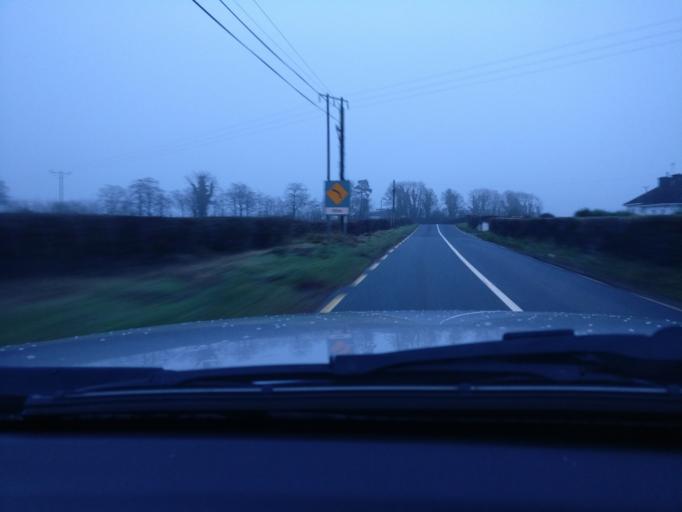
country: IE
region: Leinster
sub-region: An Mhi
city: Ballivor
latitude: 53.6110
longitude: -7.0440
